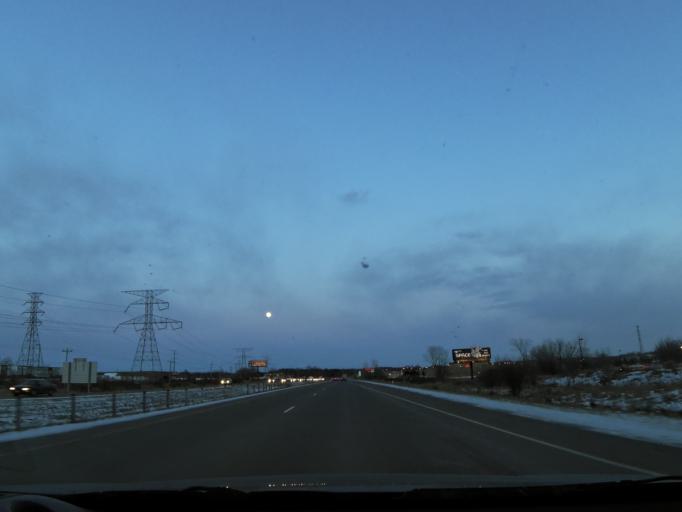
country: US
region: Minnesota
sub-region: Ramsey County
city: North Saint Paul
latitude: 45.0334
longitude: -92.9787
